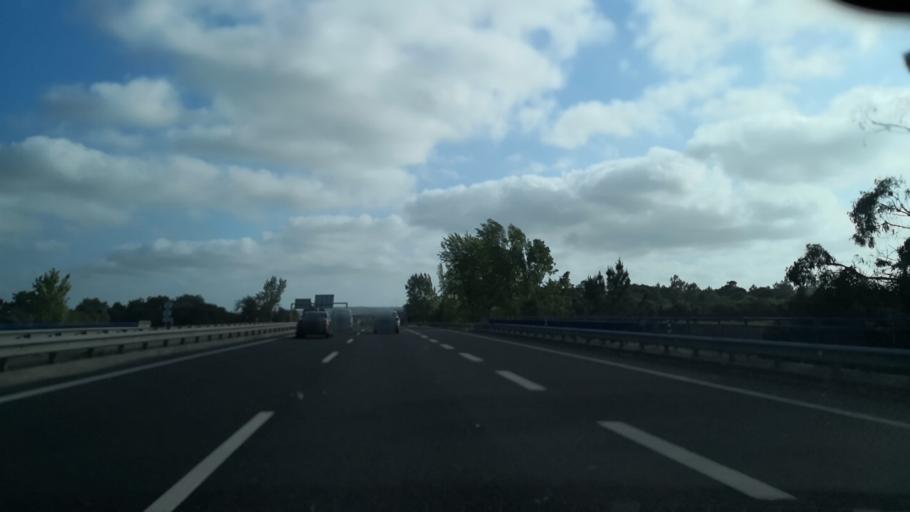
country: PT
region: Leiria
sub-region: Bombarral
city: Bombarral
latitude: 39.2877
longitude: -9.1600
